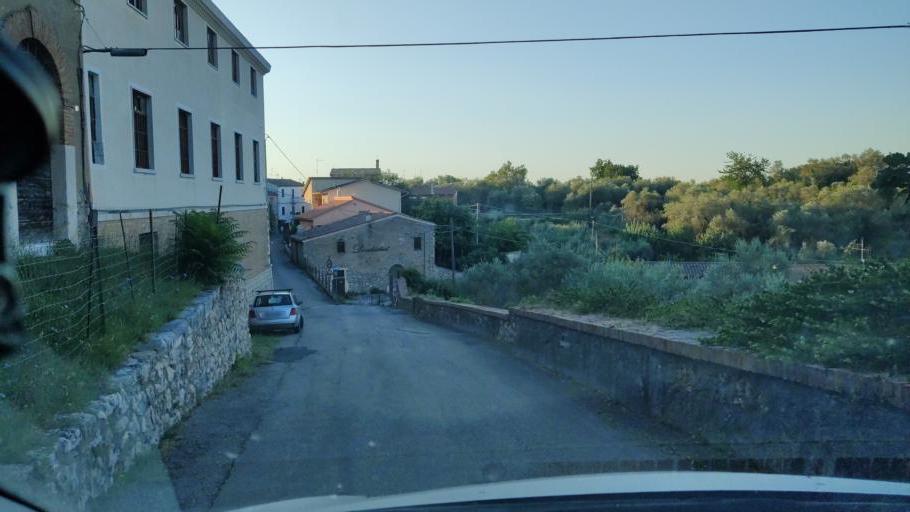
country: IT
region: Umbria
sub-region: Provincia di Terni
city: Giove
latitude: 42.5088
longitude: 12.3247
